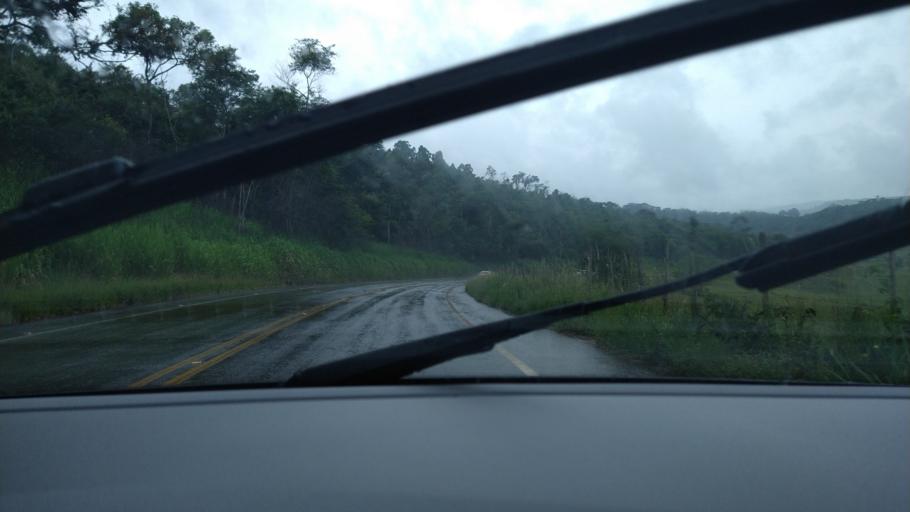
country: BR
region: Minas Gerais
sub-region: Vicosa
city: Vicosa
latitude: -20.6097
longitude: -42.8683
